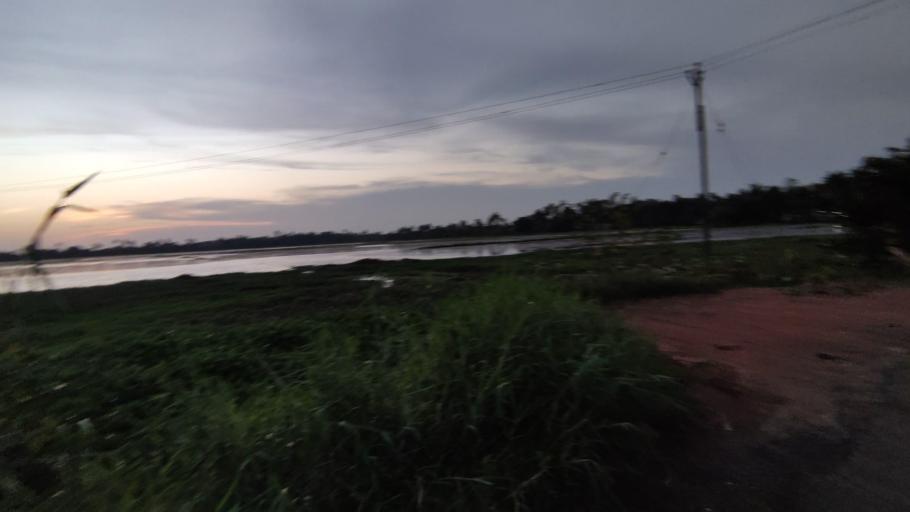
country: IN
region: Kerala
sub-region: Kottayam
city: Kottayam
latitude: 9.5719
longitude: 76.4352
